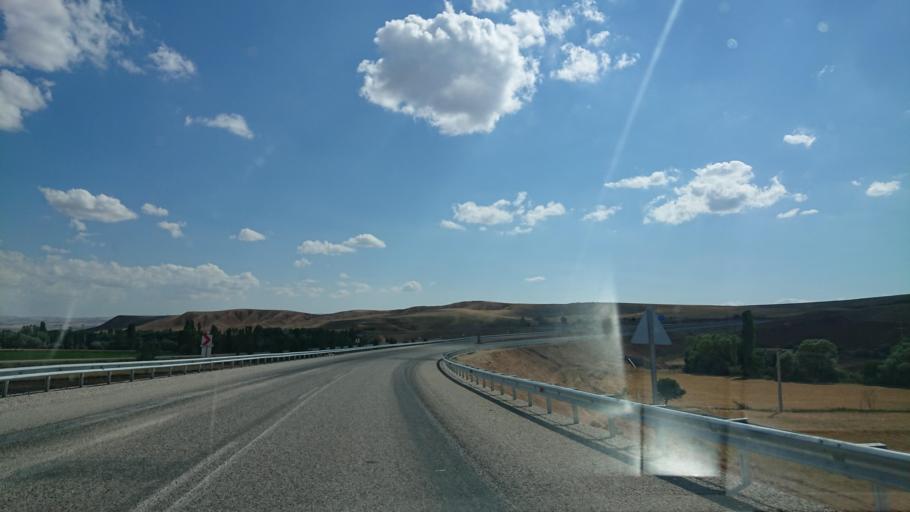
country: TR
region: Ankara
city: Evren
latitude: 39.1033
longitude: 33.9102
